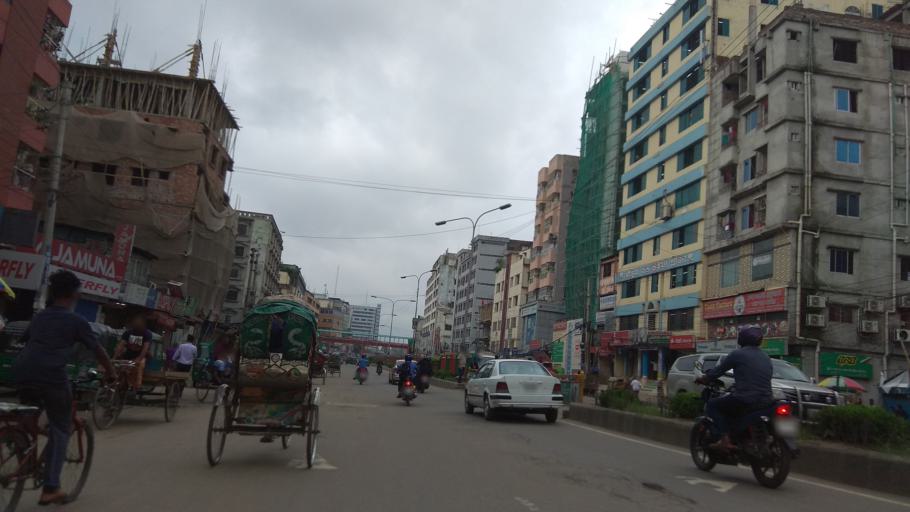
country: BD
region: Dhaka
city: Paltan
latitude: 23.7961
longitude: 90.3877
